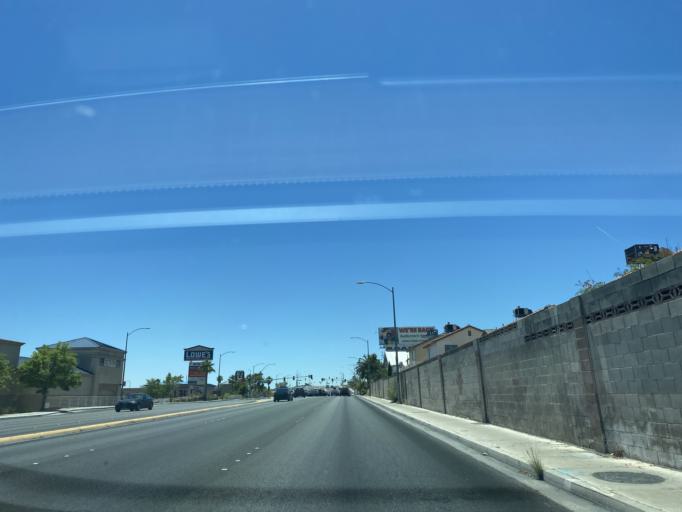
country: US
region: Nevada
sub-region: Clark County
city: Spring Valley
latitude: 36.1834
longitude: -115.2601
